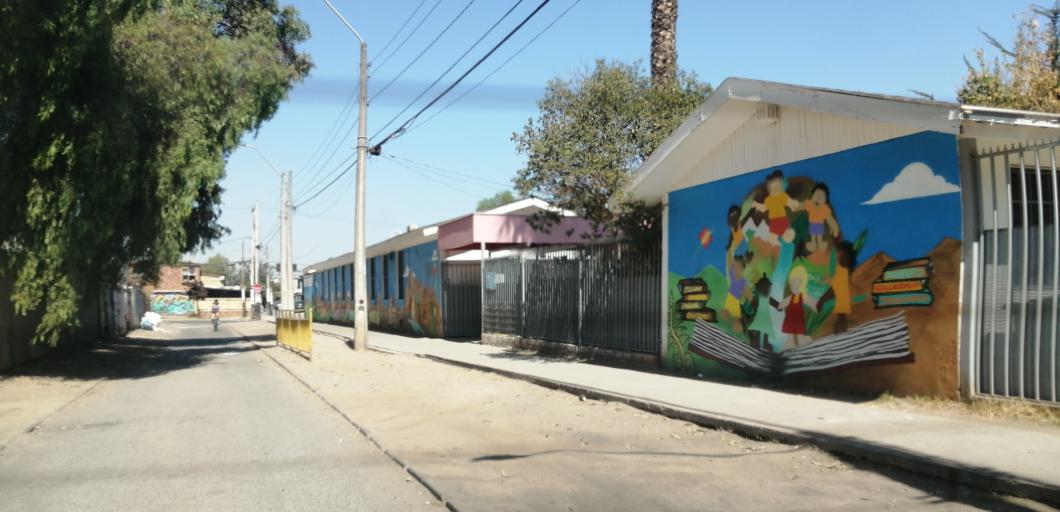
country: CL
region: Santiago Metropolitan
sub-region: Provincia de Santiago
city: Lo Prado
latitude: -33.4332
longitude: -70.7414
